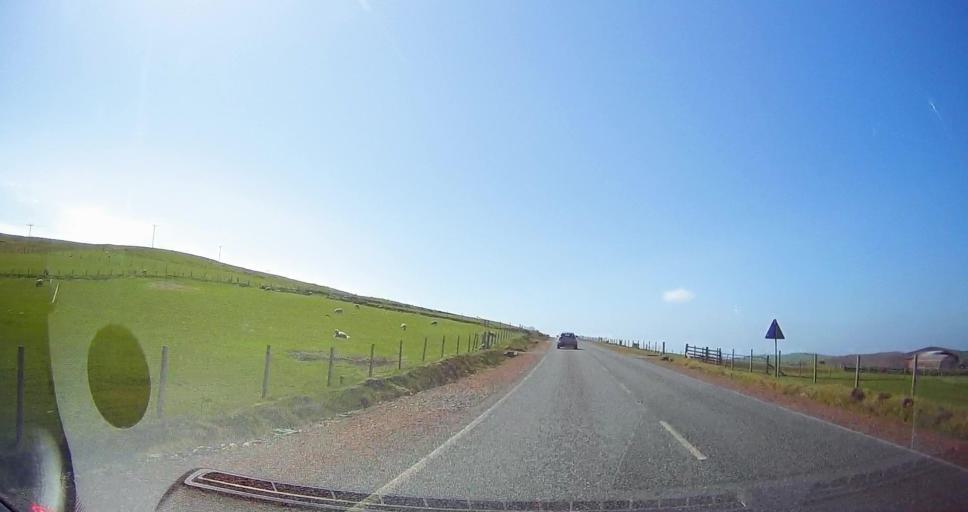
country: GB
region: Scotland
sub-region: Shetland Islands
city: Sandwick
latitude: 60.1165
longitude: -1.2927
